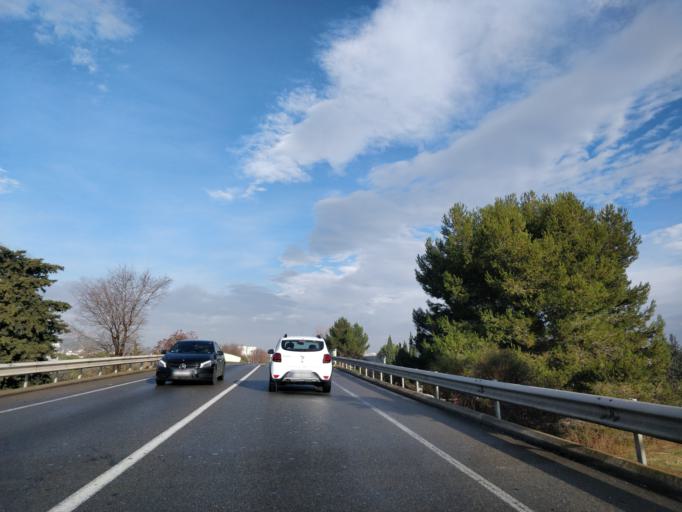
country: FR
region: Languedoc-Roussillon
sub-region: Departement du Gard
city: Nimes
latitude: 43.8117
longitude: 4.3546
